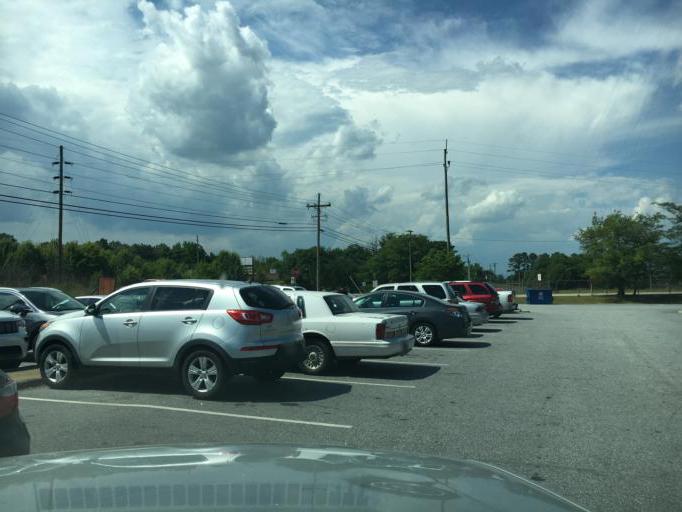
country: US
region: South Carolina
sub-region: Spartanburg County
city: Southern Shops
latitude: 34.9732
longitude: -81.9980
